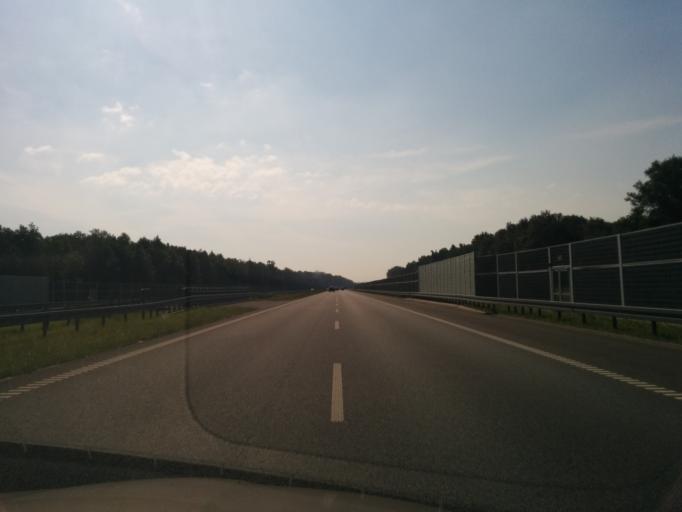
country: PL
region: Silesian Voivodeship
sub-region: Powiat tarnogorski
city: Radzionkow
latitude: 50.3822
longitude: 18.8618
